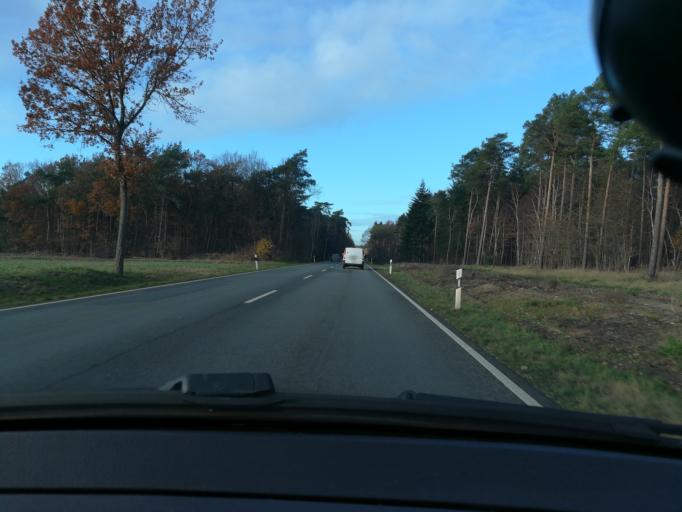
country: DE
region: Lower Saxony
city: Uchte
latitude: 52.5334
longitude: 8.8779
